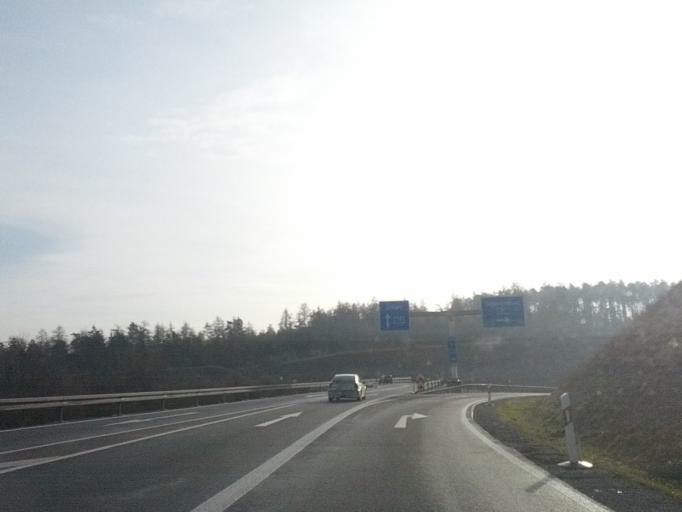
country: DE
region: Thuringia
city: Rohr
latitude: 50.5785
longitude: 10.4806
